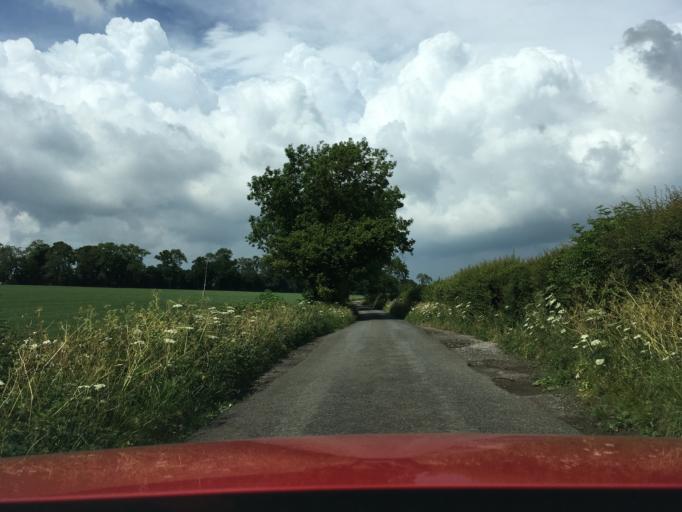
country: GB
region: England
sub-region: Gloucestershire
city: Chalford
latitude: 51.6995
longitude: -2.1102
